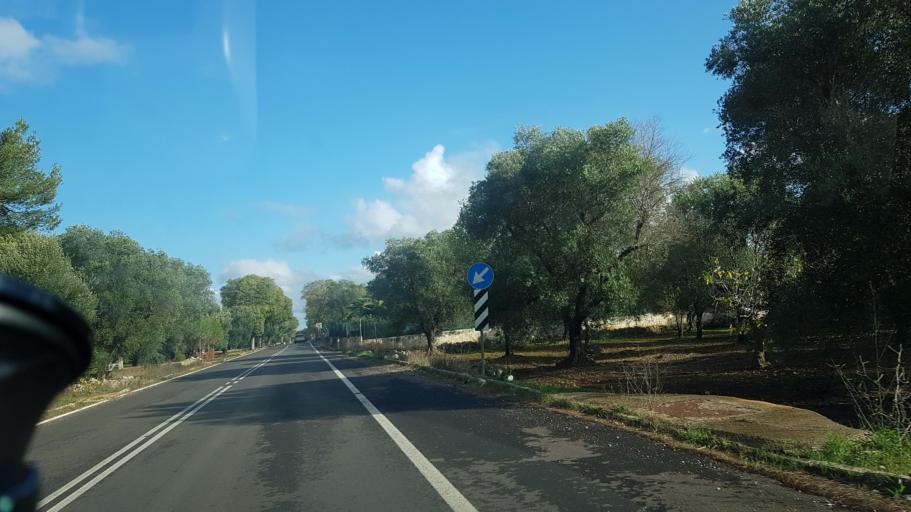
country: IT
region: Apulia
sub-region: Provincia di Brindisi
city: San Michele Salentino
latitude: 40.6465
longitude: 17.6106
